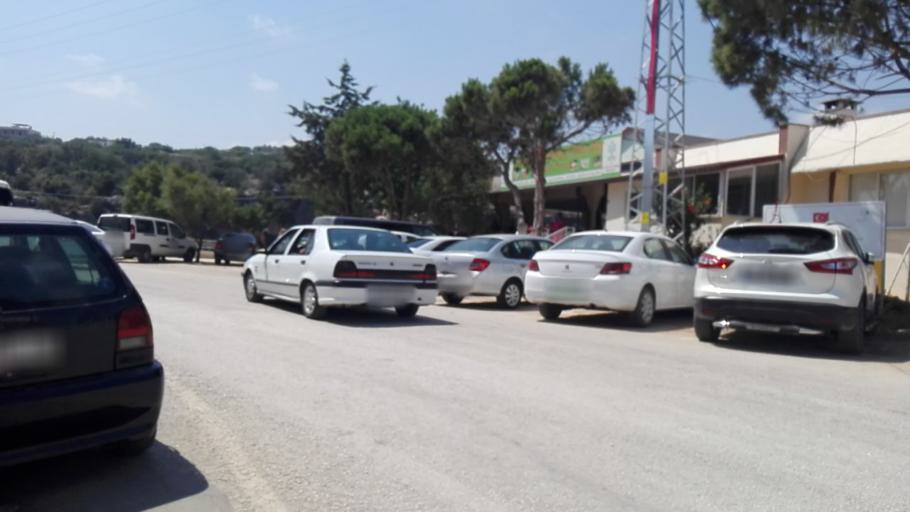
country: TR
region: Mersin
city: Silifke
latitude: 36.4517
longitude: 34.1060
